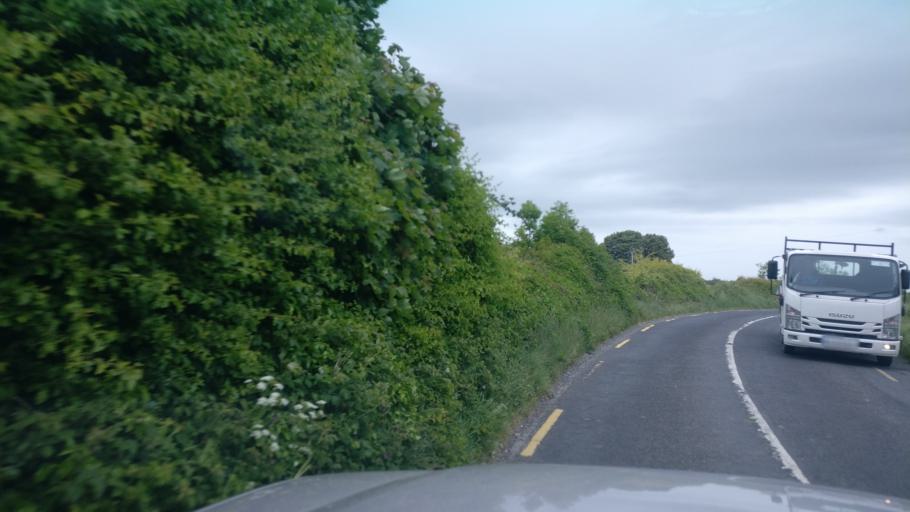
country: IE
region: Connaught
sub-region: County Galway
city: Loughrea
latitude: 53.0944
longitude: -8.4390
